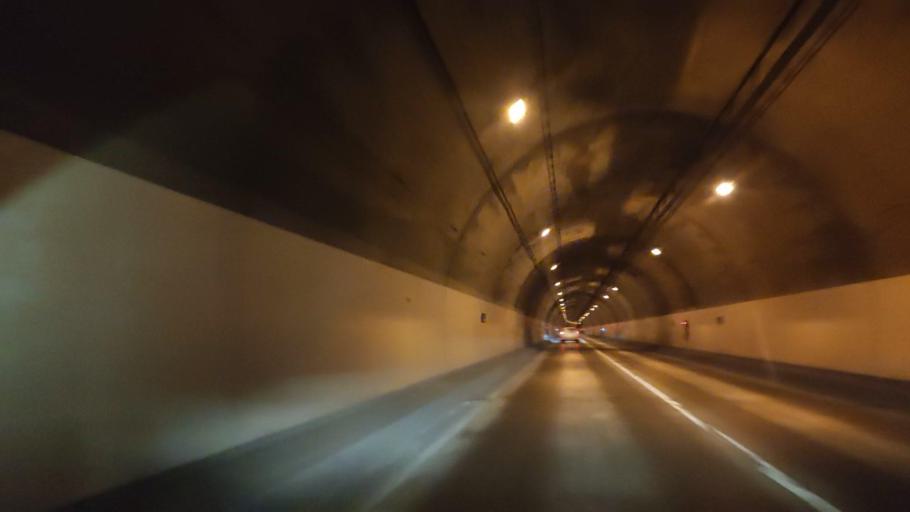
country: JP
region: Hokkaido
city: Ishikari
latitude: 43.4583
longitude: 141.4068
